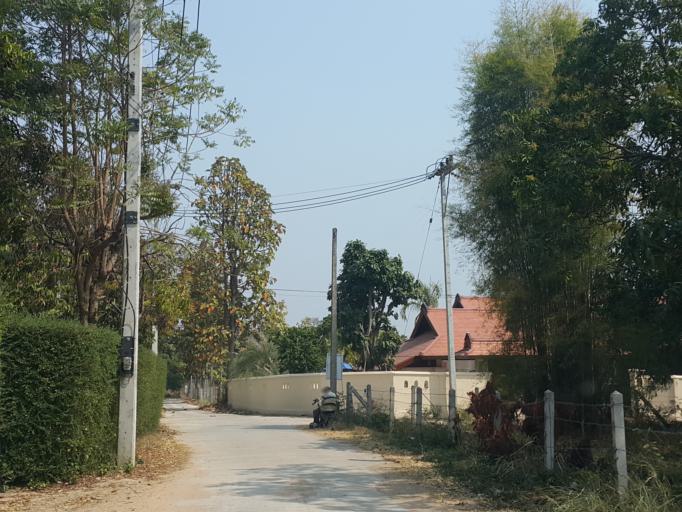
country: TH
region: Chiang Mai
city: Hang Dong
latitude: 18.6809
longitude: 98.8774
